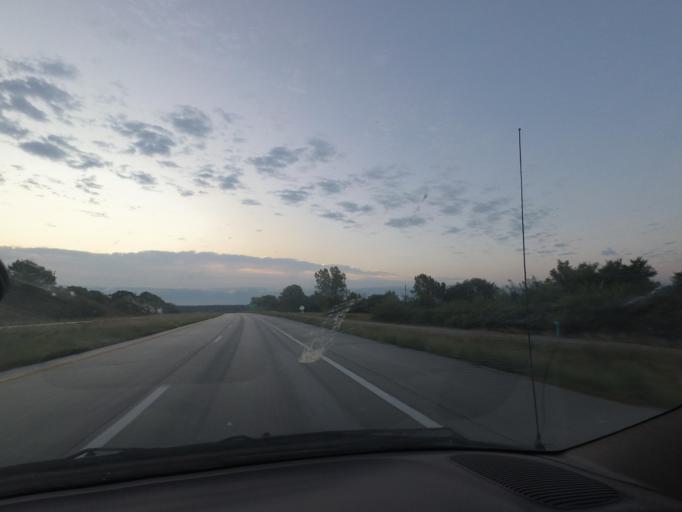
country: US
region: Missouri
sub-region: Macon County
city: Macon
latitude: 39.7505
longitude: -92.5282
